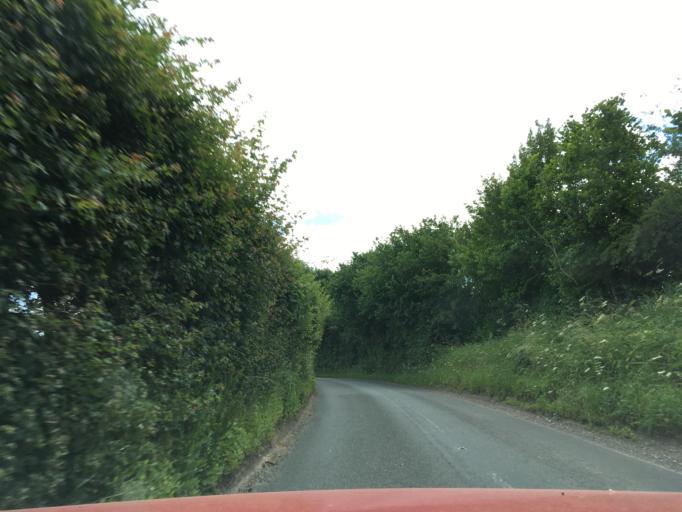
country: GB
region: England
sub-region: West Berkshire
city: Winterbourne
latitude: 51.4295
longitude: -1.3810
